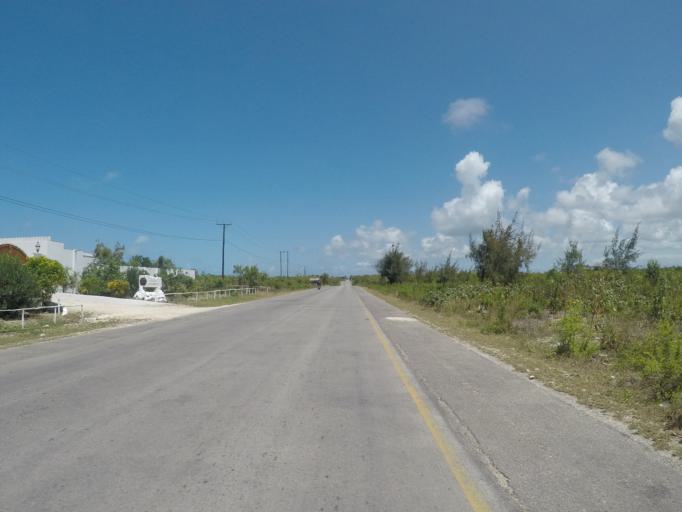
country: TZ
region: Zanzibar Central/South
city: Nganane
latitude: -6.2895
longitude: 39.5368
